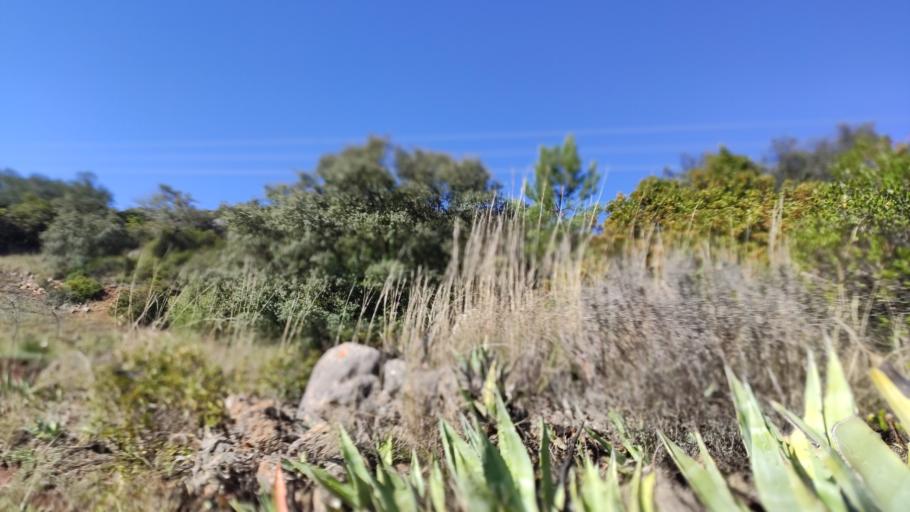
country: PT
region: Faro
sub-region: Sao Bras de Alportel
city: Sao Bras de Alportel
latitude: 37.1562
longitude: -7.9082
